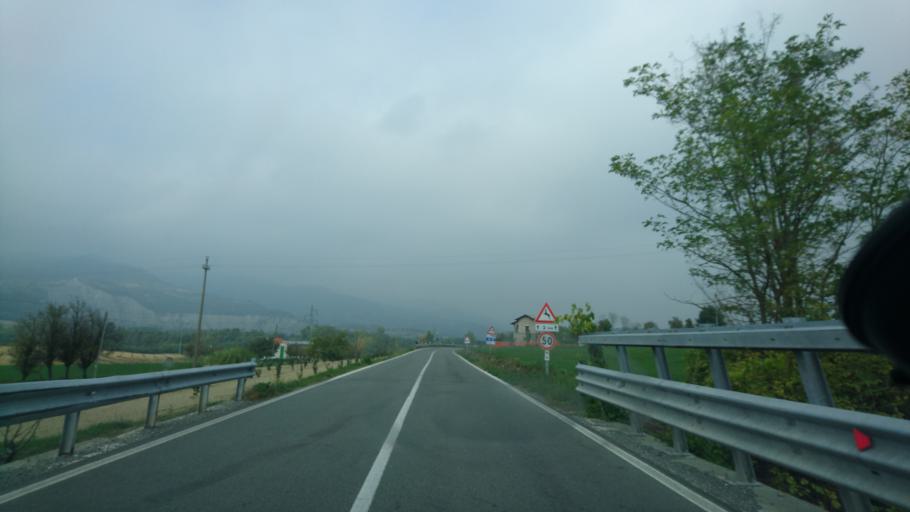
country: IT
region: Piedmont
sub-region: Provincia di Asti
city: Mombaldone
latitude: 44.5651
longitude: 8.3460
